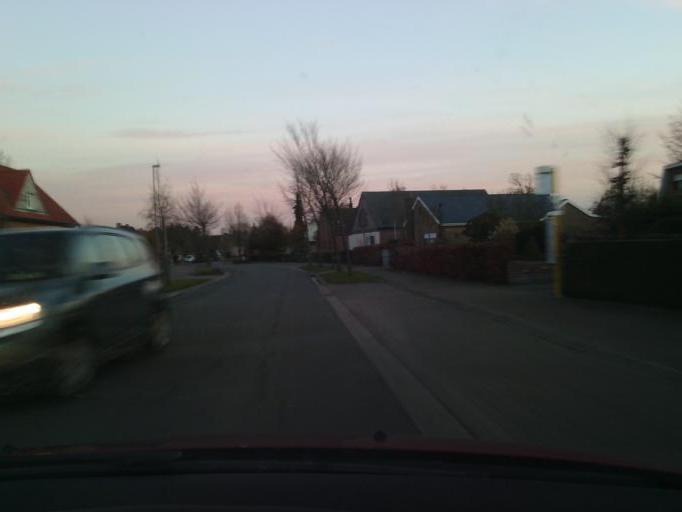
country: BE
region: Flanders
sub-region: Provincie Oost-Vlaanderen
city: Berlare
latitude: 51.0611
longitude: 4.0048
